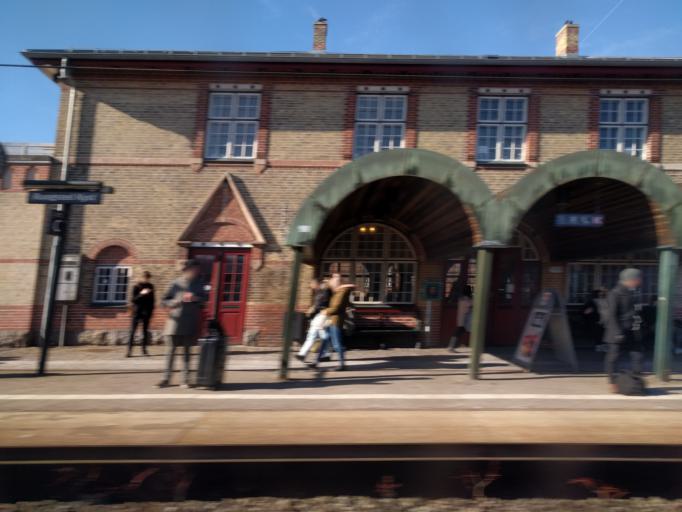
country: DK
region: Capital Region
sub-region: Horsholm Kommune
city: Horsholm
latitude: 55.8825
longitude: 12.5316
